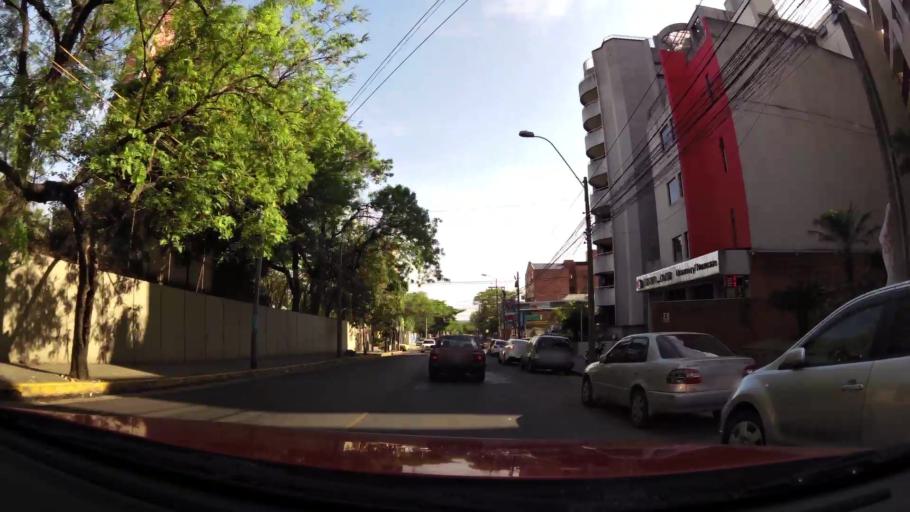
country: PY
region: Asuncion
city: Asuncion
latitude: -25.2852
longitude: -57.6165
